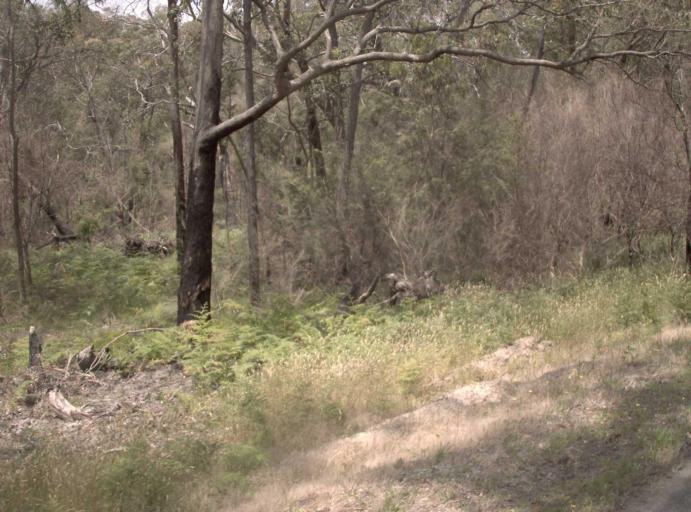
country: AU
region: Victoria
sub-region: Latrobe
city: Traralgon
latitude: -38.2674
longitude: 146.6917
